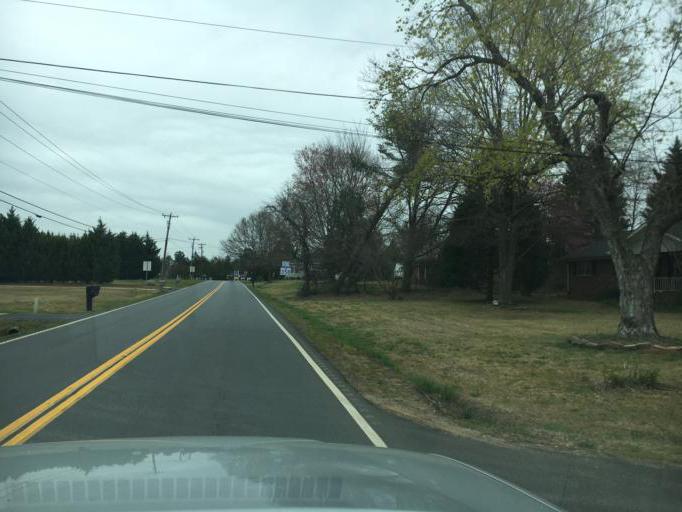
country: US
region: South Carolina
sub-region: Spartanburg County
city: Lyman
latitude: 34.9628
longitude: -82.1410
